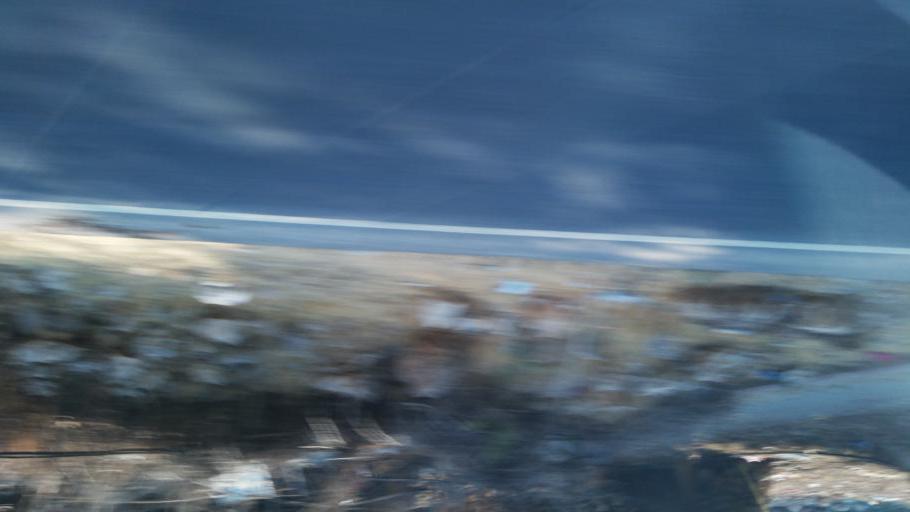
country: TR
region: Mardin
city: Sivrice
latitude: 37.2238
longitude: 41.3305
